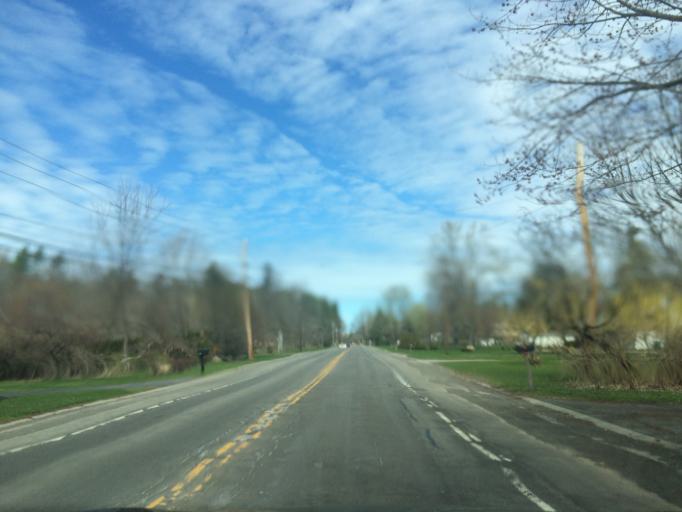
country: US
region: New York
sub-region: Monroe County
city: East Rochester
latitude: 43.0892
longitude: -77.4887
